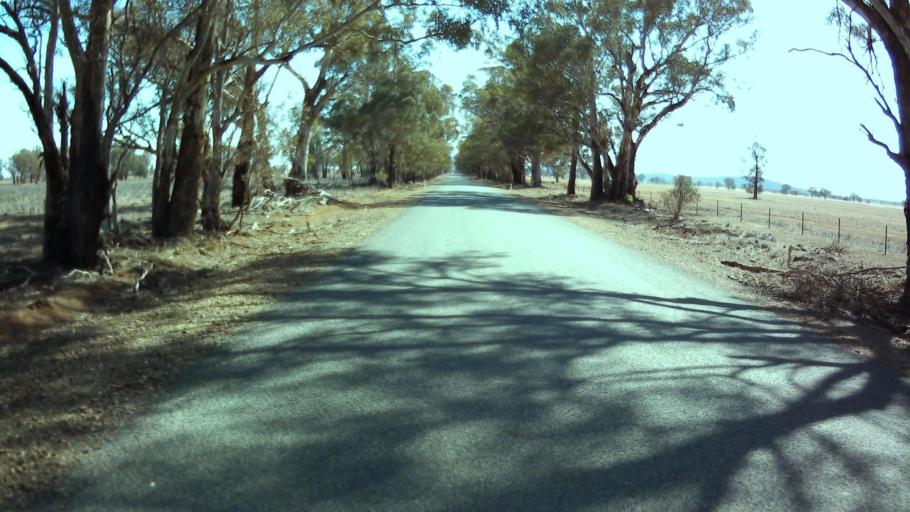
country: AU
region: New South Wales
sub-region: Weddin
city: Grenfell
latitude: -33.7237
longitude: 147.8963
